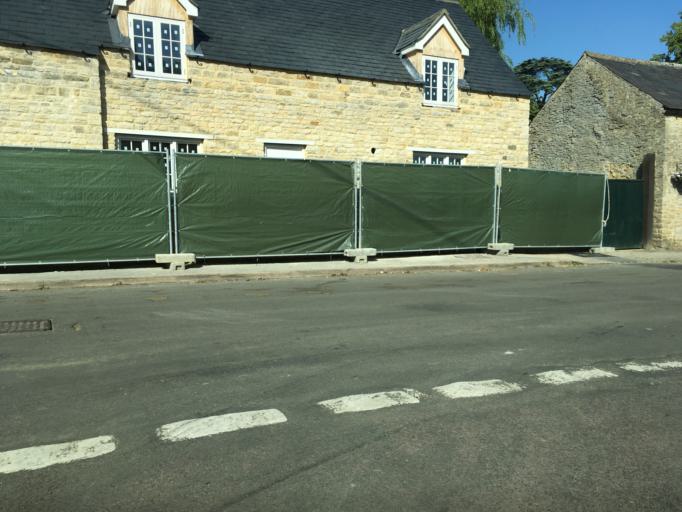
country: GB
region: England
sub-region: Oxfordshire
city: Bicester
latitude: 51.9305
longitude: -1.1173
